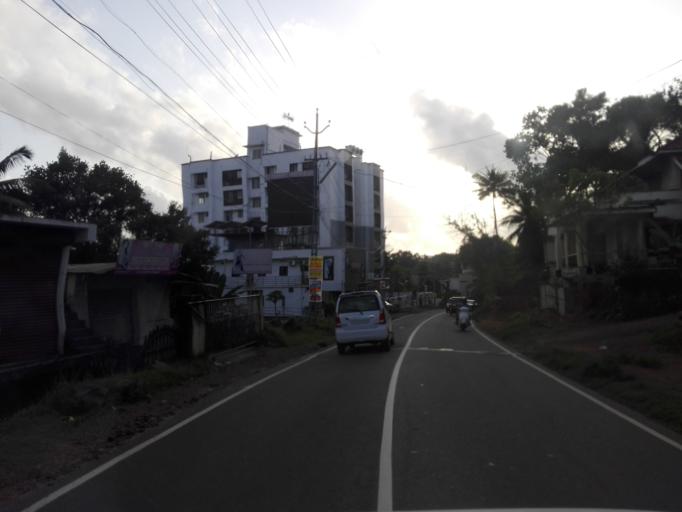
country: IN
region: Kerala
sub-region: Kottayam
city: Kottayam
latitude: 9.5947
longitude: 76.5149
